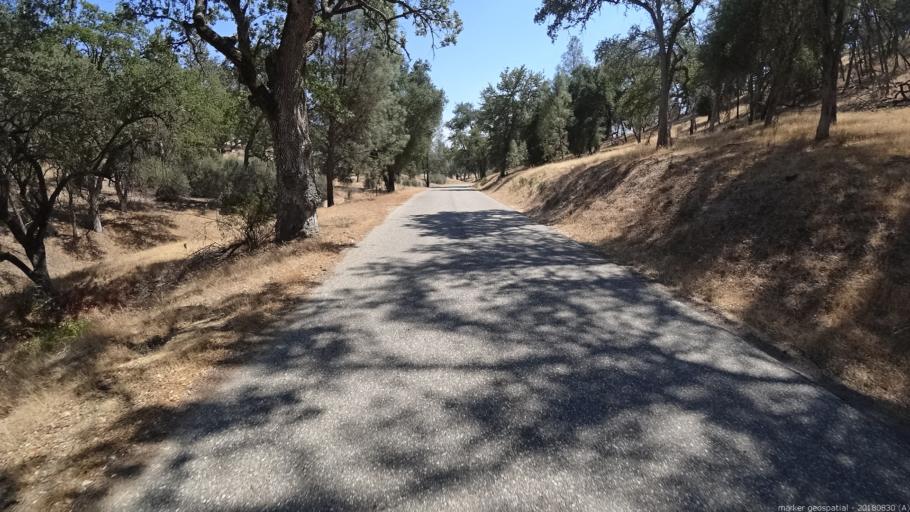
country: US
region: California
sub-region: Monterey County
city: King City
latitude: 35.9887
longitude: -121.2611
